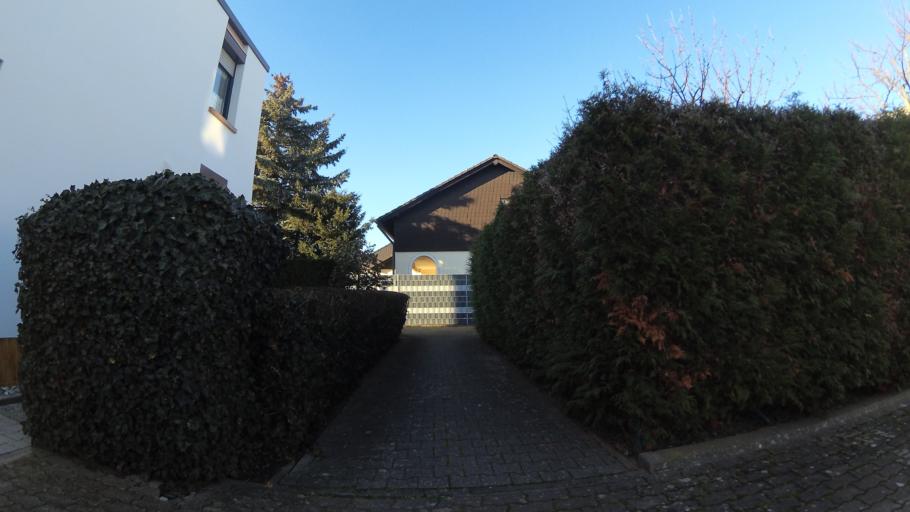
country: DE
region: Saarland
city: Saarwellingen
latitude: 49.3366
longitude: 6.7812
